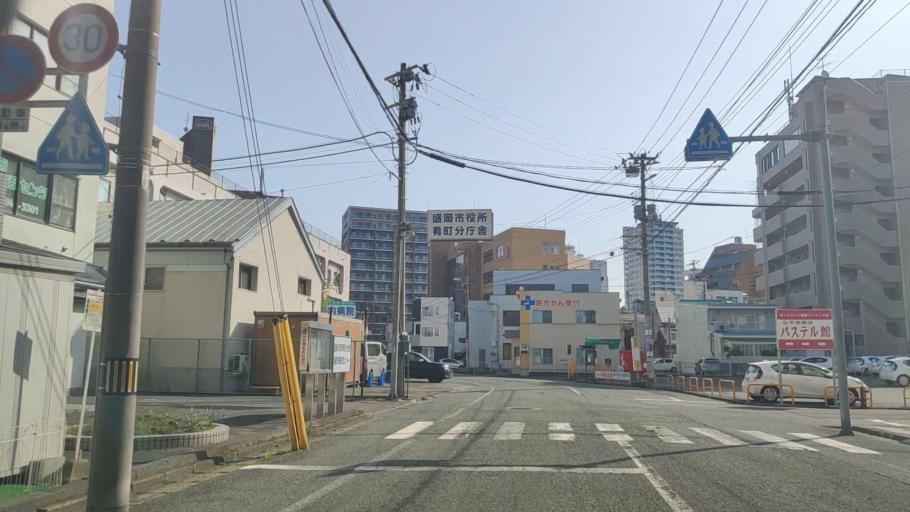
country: JP
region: Iwate
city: Morioka-shi
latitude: 39.6978
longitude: 141.1528
